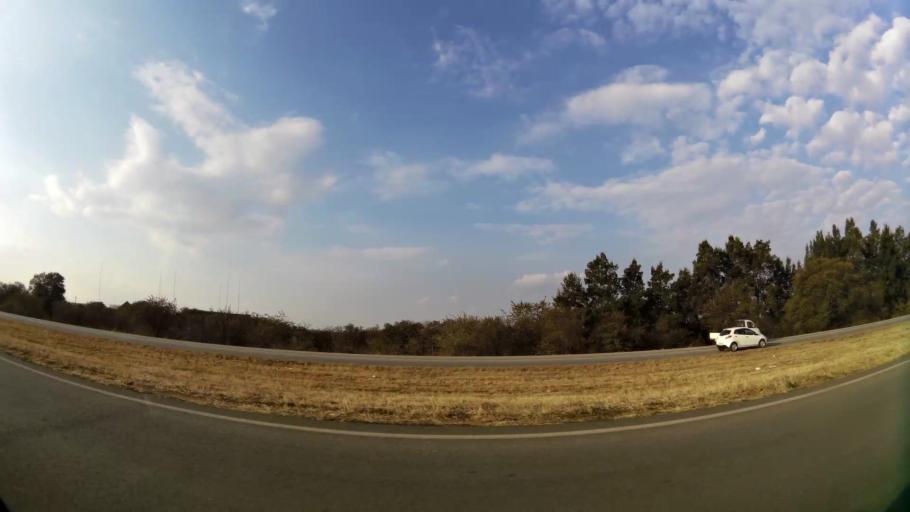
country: ZA
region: Gauteng
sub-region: Sedibeng District Municipality
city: Vereeniging
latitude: -26.6265
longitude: 27.8655
